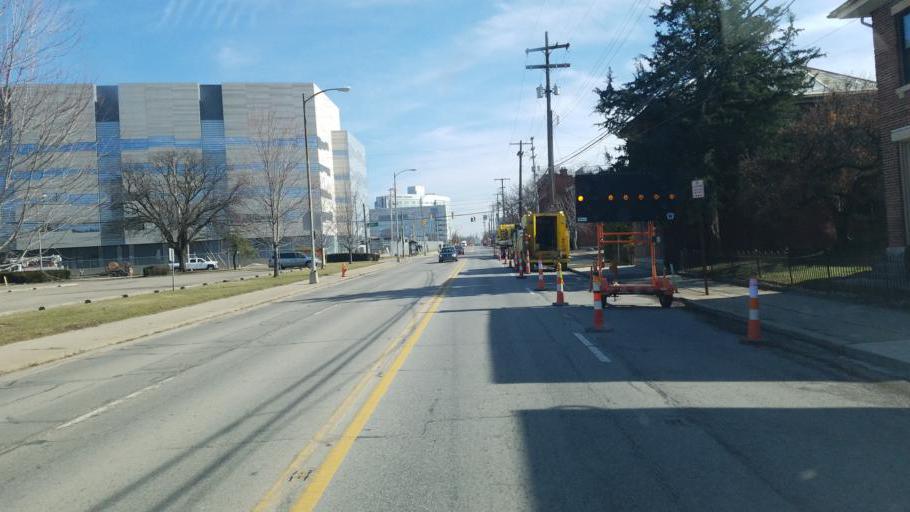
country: US
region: Ohio
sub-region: Franklin County
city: Columbus
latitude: 39.9525
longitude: -82.9902
